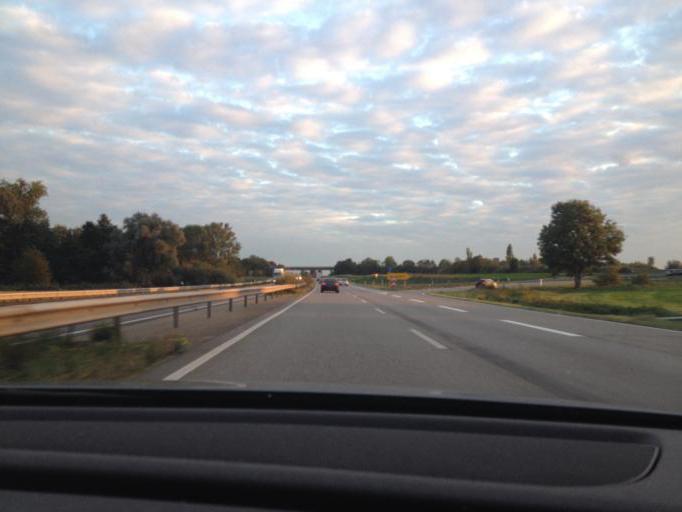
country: DE
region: Rheinland-Pfalz
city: Neuhofen
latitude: 49.4066
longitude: 8.4105
